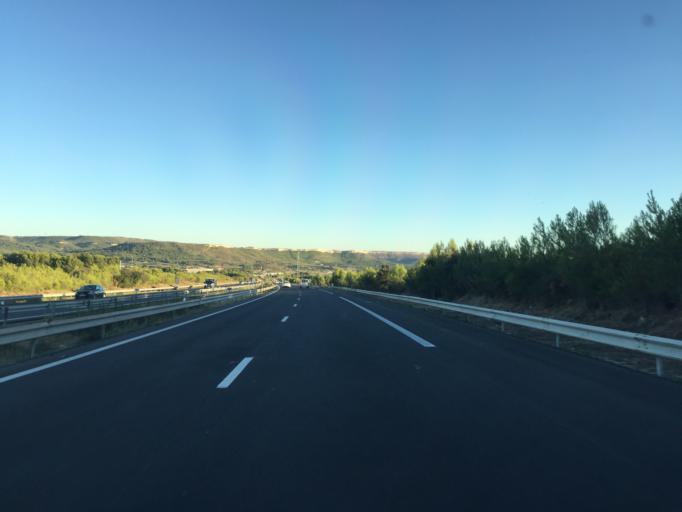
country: FR
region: Provence-Alpes-Cote d'Azur
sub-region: Departement des Bouches-du-Rhone
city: La Fare-les-Oliviers
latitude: 43.5270
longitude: 5.2204
